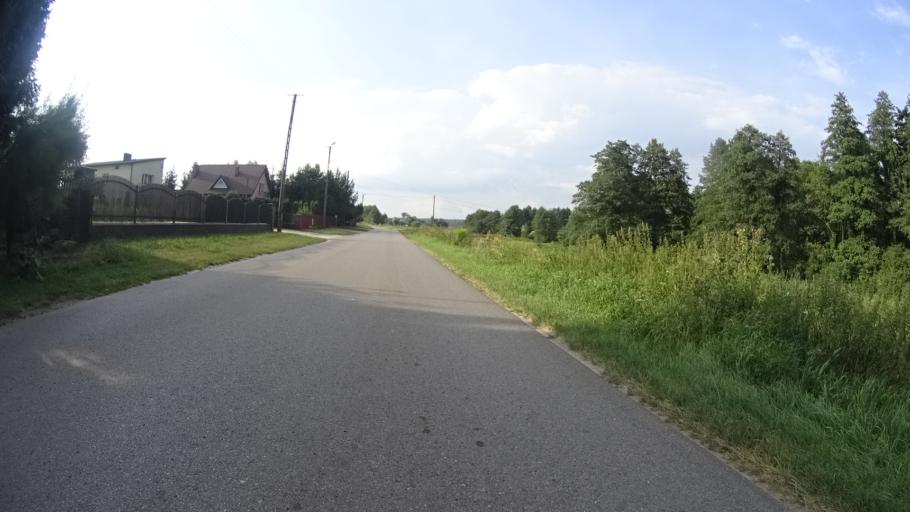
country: PL
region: Masovian Voivodeship
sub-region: Powiat grojecki
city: Mogielnica
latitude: 51.6791
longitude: 20.7338
